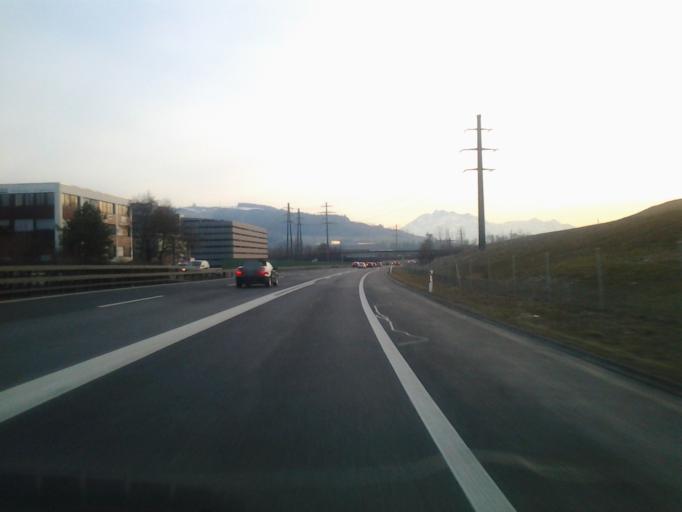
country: CH
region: Zug
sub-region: Zug
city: Hunenberg
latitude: 47.1528
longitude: 8.4309
